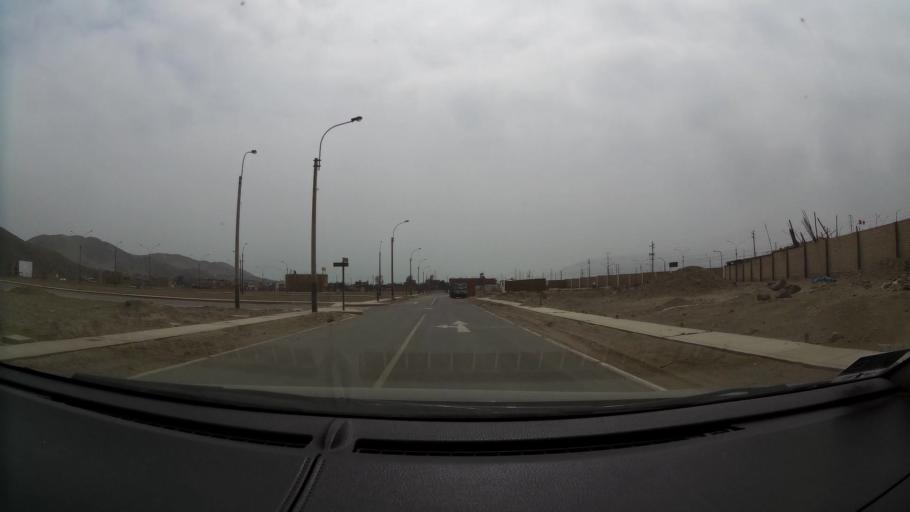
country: PE
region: Lima
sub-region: Lima
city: Santa Rosa
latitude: -11.7921
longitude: -77.1487
